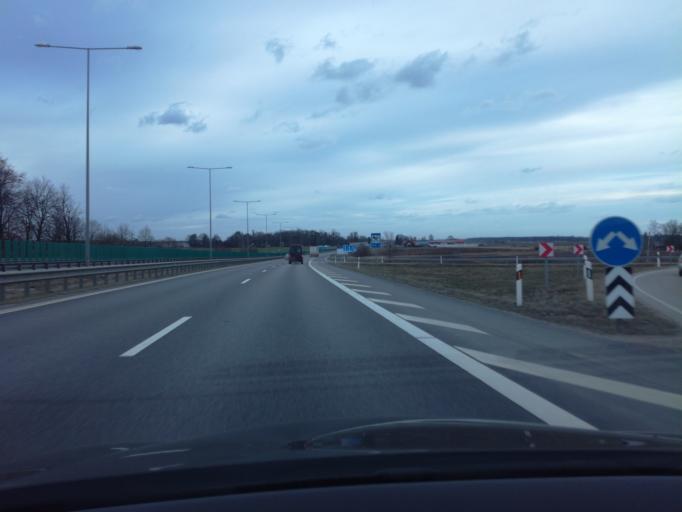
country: LT
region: Kauno apskritis
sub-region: Kauno rajonas
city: Mastaiciai
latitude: 54.7832
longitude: 23.7828
